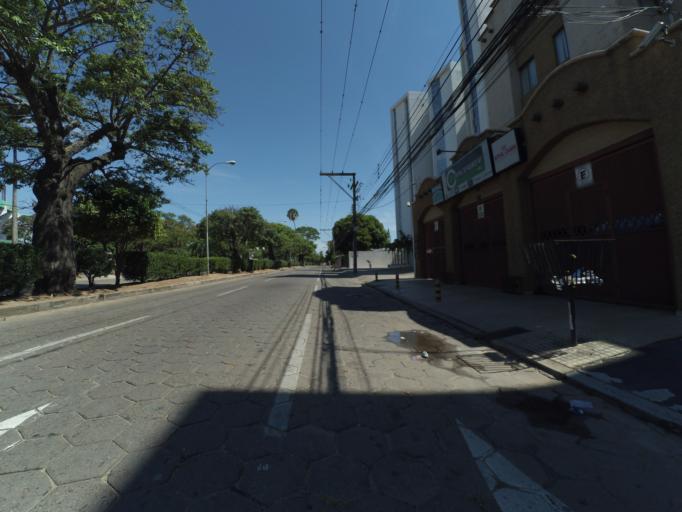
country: BO
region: Santa Cruz
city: Santa Cruz de la Sierra
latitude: -17.7960
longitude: -63.1822
